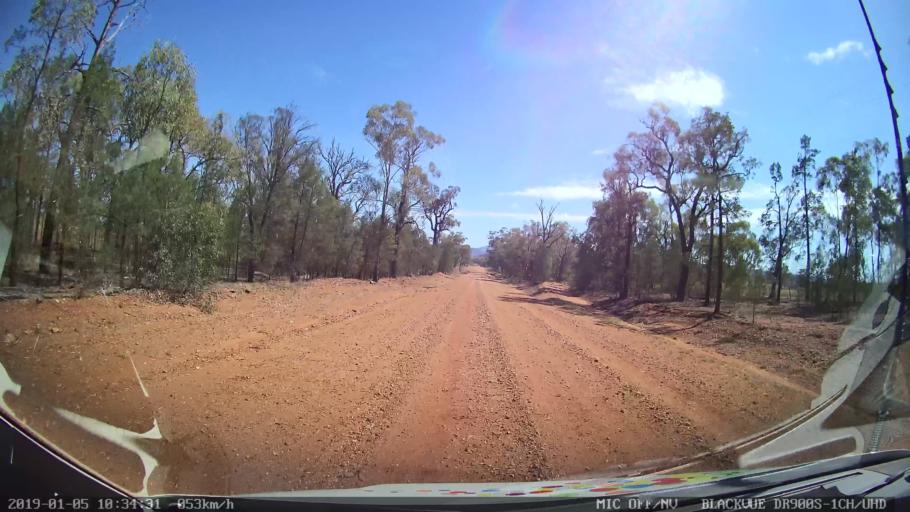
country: AU
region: New South Wales
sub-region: Gilgandra
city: Gilgandra
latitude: -31.4977
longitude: 148.9291
